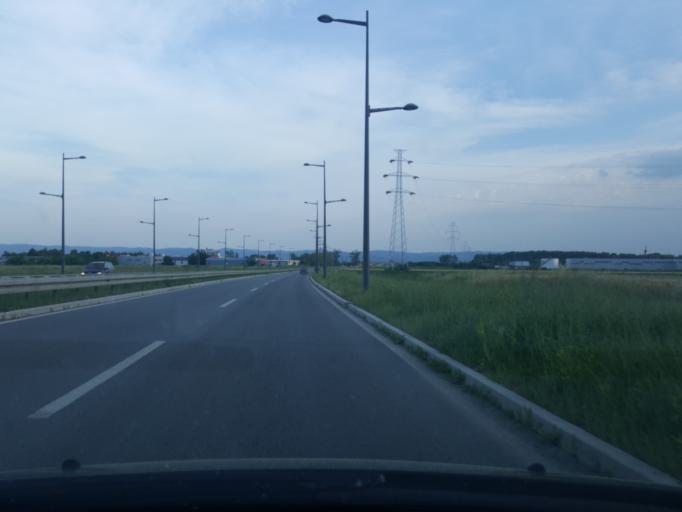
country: RS
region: Autonomna Pokrajina Vojvodina
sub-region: Juznobacki Okrug
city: Novi Sad
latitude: 45.2939
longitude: 19.8076
